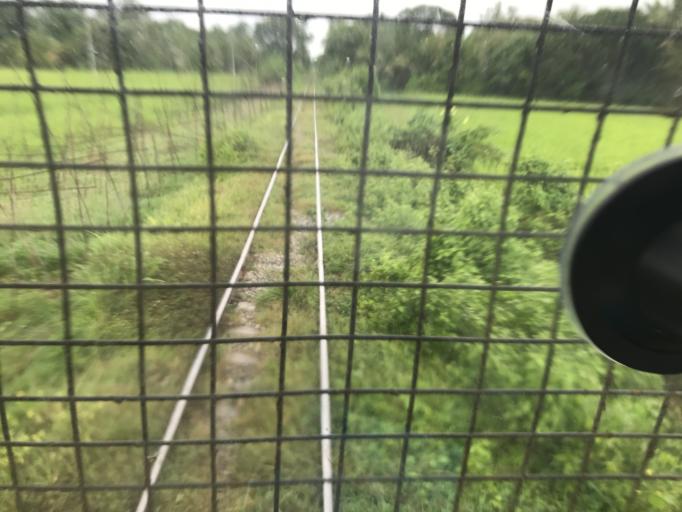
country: MM
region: Bago
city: Pyay
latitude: 18.7303
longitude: 95.3631
